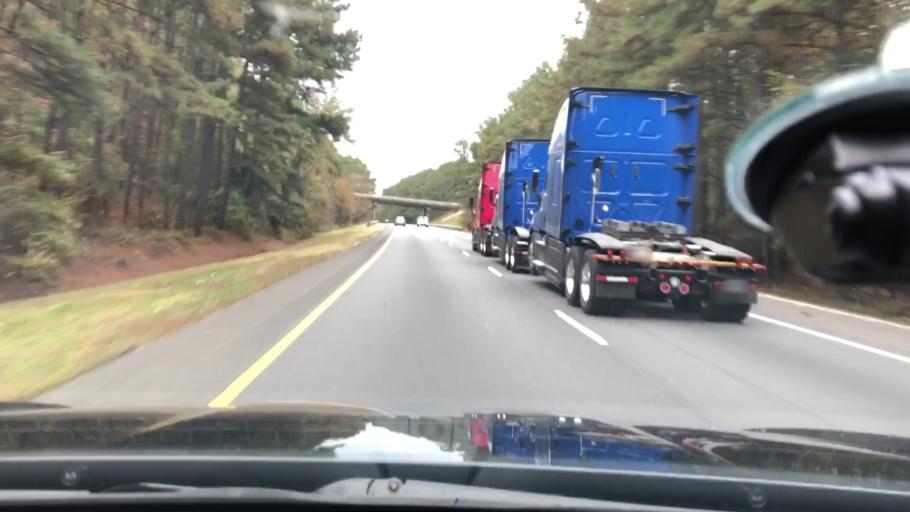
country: US
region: Arkansas
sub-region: Hot Spring County
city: Malvern
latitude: 34.2858
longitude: -92.9558
